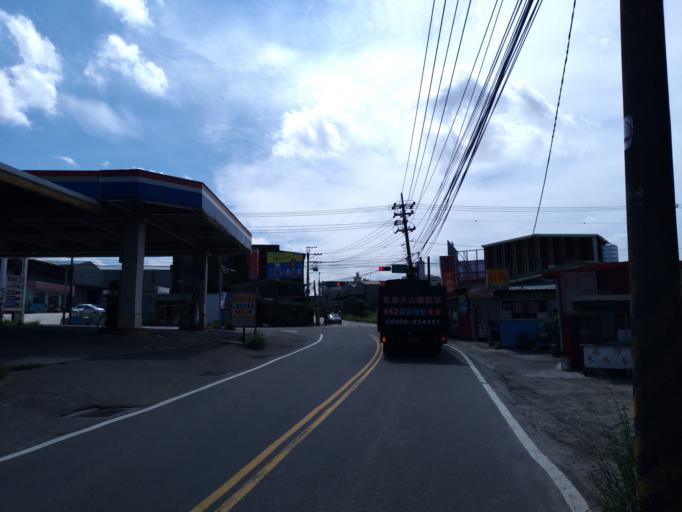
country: TW
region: Taiwan
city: Daxi
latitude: 24.9458
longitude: 121.1474
